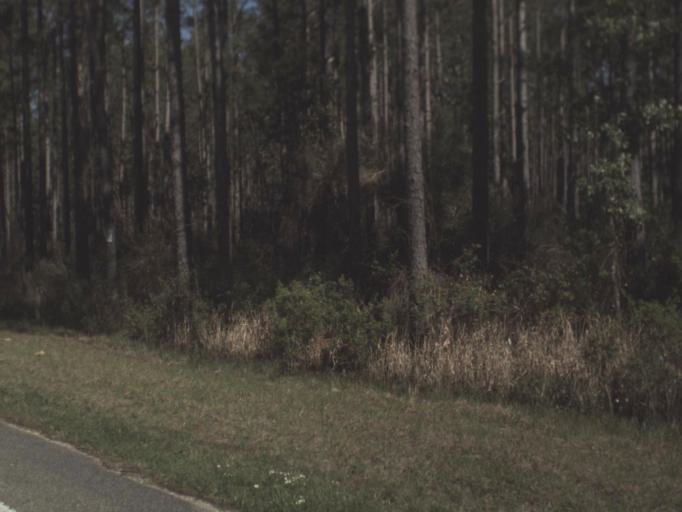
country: US
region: Florida
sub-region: Gulf County
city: Port Saint Joe
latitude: 29.8377
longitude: -85.2728
